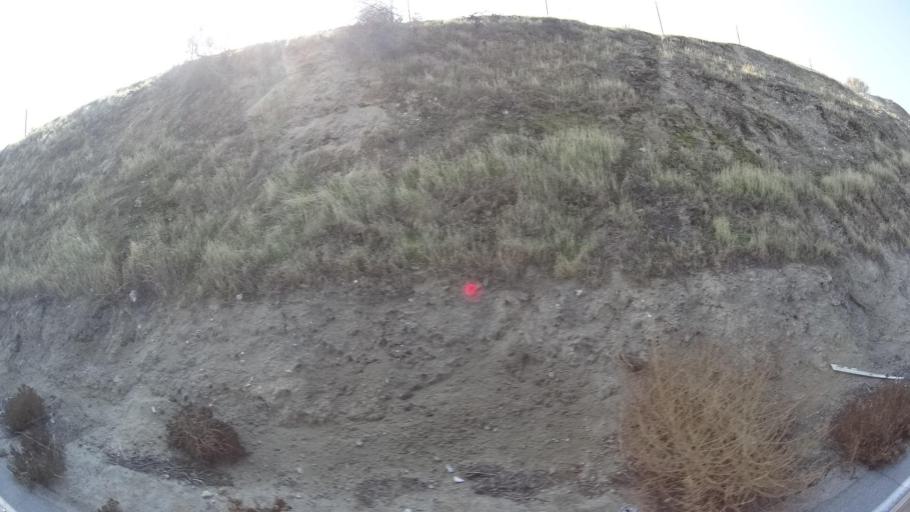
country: US
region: California
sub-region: Kern County
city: Ford City
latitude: 35.2710
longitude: -119.3149
